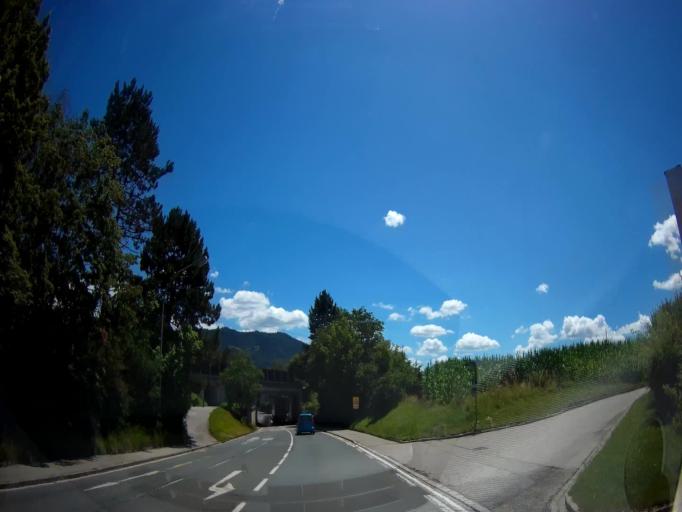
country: AT
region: Carinthia
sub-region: Politischer Bezirk Sankt Veit an der Glan
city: Sankt Veit an der Glan
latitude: 46.7502
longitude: 14.3805
